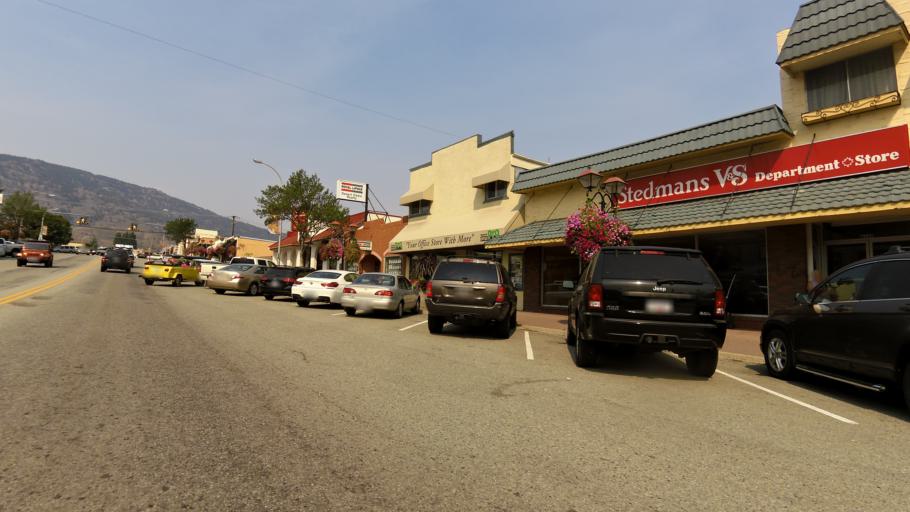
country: CA
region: British Columbia
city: Osoyoos
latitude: 49.0329
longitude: -119.4657
